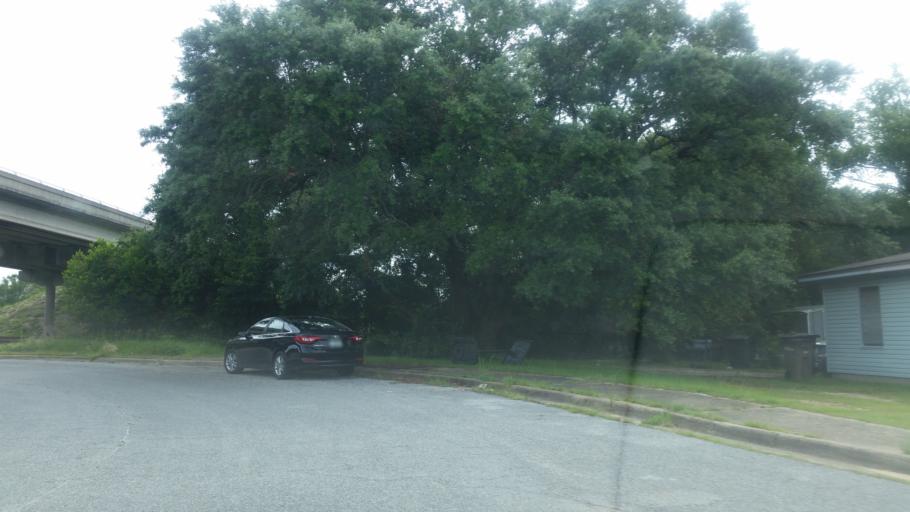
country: US
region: Florida
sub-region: Escambia County
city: Goulding
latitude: 30.4462
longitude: -87.2241
